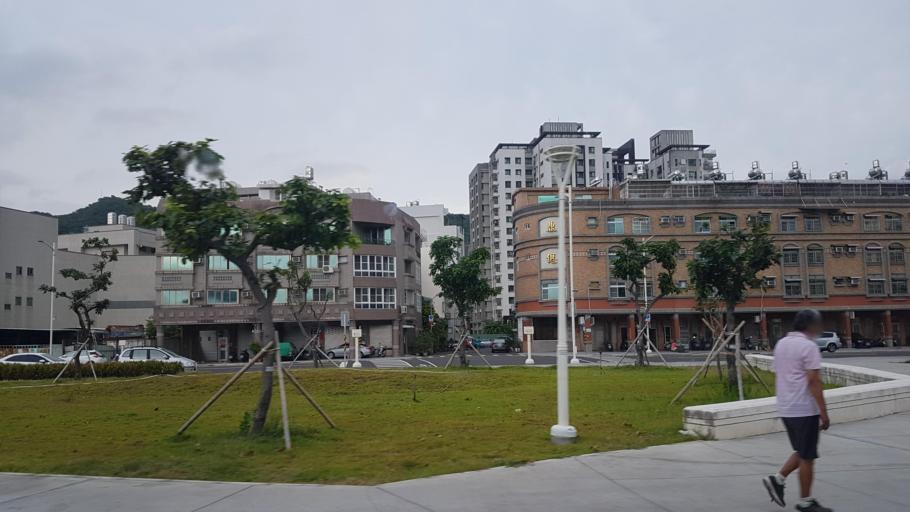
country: TW
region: Kaohsiung
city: Kaohsiung
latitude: 22.6465
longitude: 120.2814
